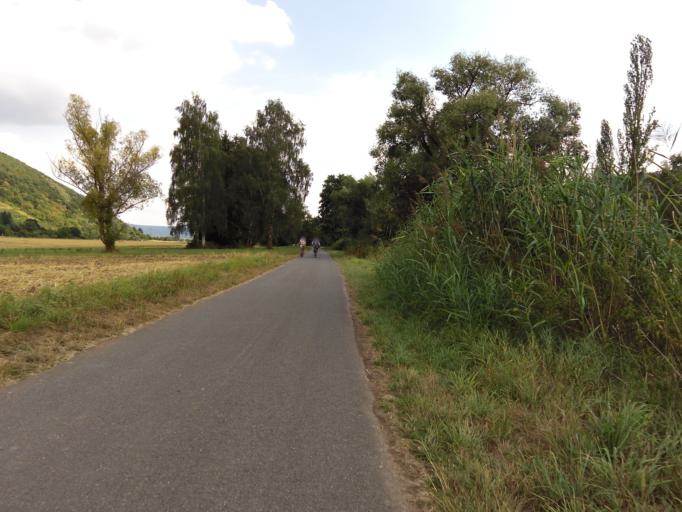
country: DE
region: Bavaria
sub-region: Regierungsbezirk Unterfranken
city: Laudenbach
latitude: 49.7410
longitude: 9.1836
